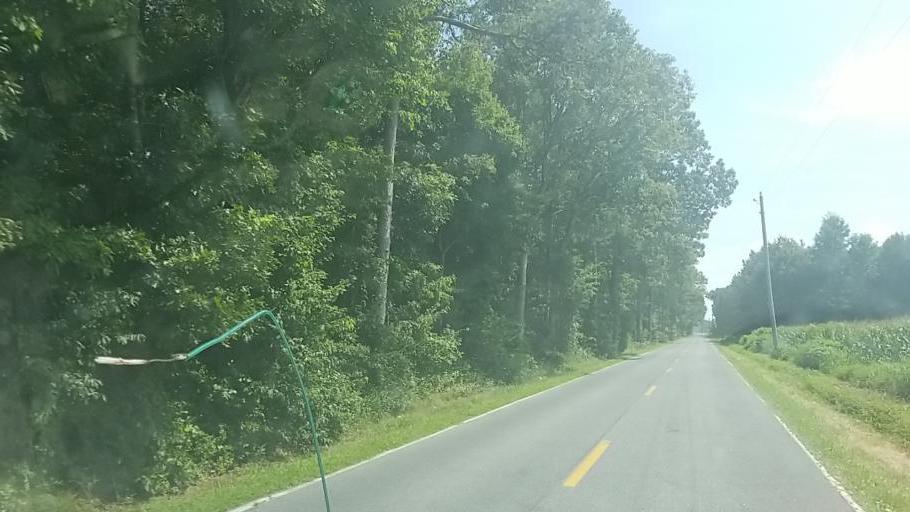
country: US
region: Maryland
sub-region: Wicomico County
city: Hebron
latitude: 38.4378
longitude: -75.6982
